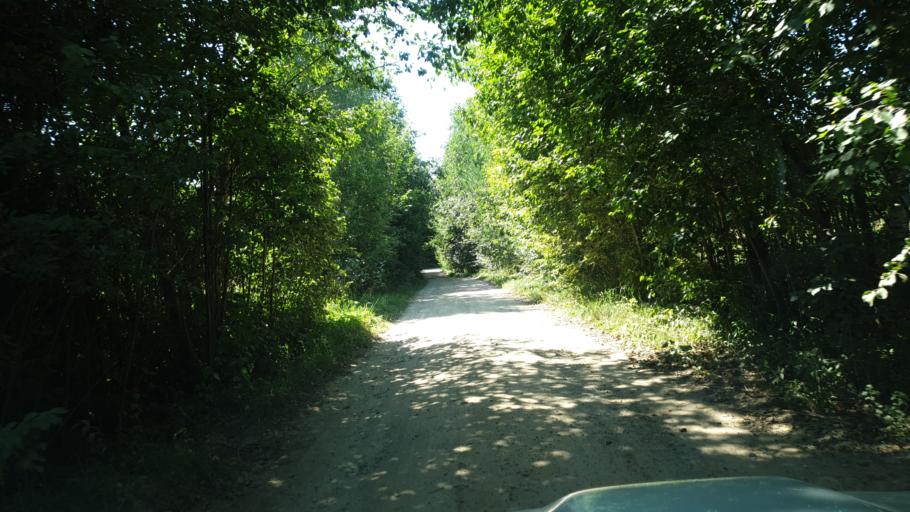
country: LT
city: Sirvintos
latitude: 54.9001
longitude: 24.9025
